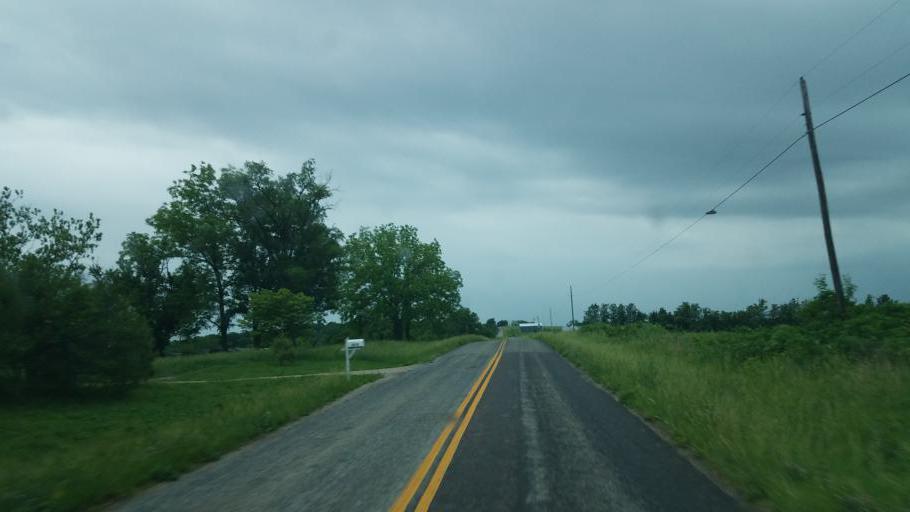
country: US
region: Missouri
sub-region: Moniteau County
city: California
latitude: 38.7692
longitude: -92.6053
